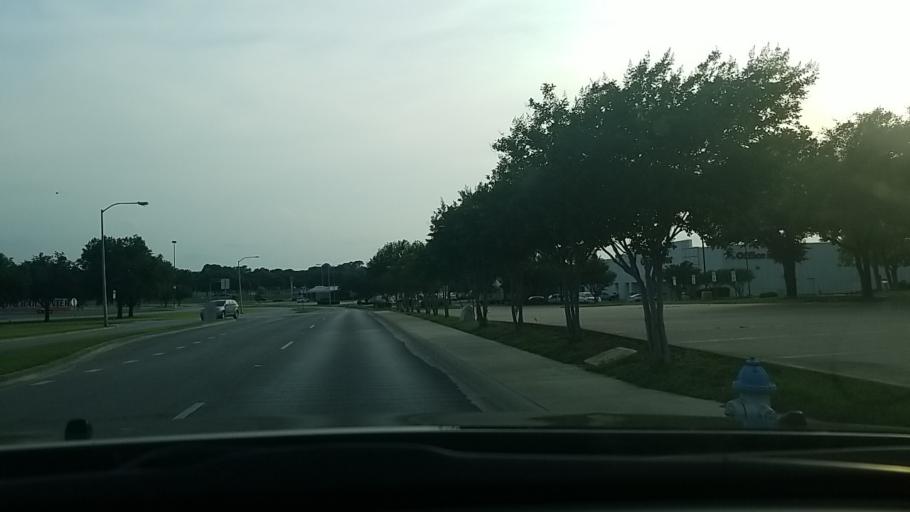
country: US
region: Texas
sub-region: Denton County
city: Denton
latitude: 33.1923
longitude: -97.1095
